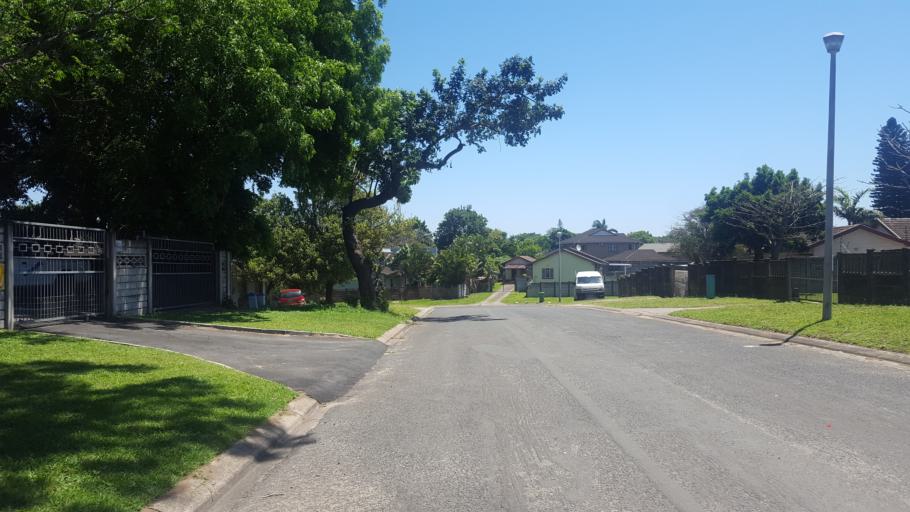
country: ZA
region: KwaZulu-Natal
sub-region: uThungulu District Municipality
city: Richards Bay
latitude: -28.7639
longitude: 32.0642
